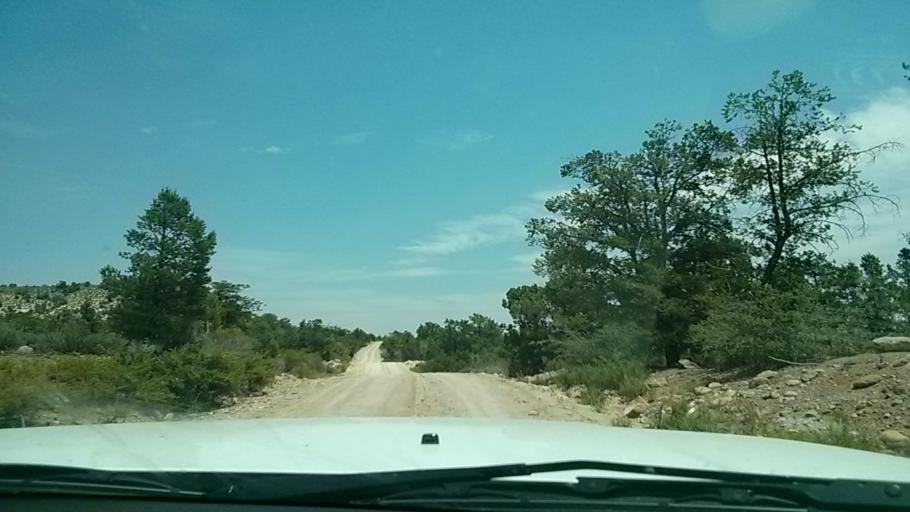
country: US
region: Utah
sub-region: Washington County
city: Washington
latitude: 37.2430
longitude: -113.4504
